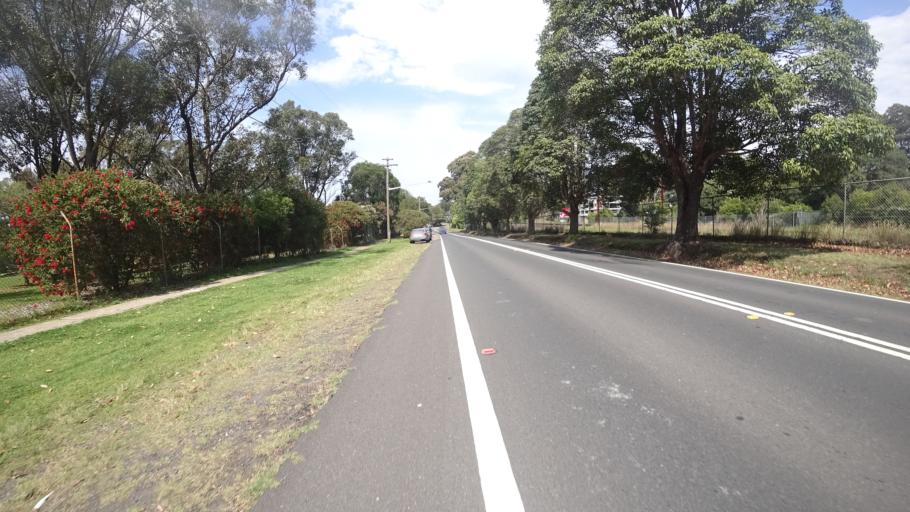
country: AU
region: New South Wales
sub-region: Hornsby Shire
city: Mount Colah
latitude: -33.6824
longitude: 151.1117
